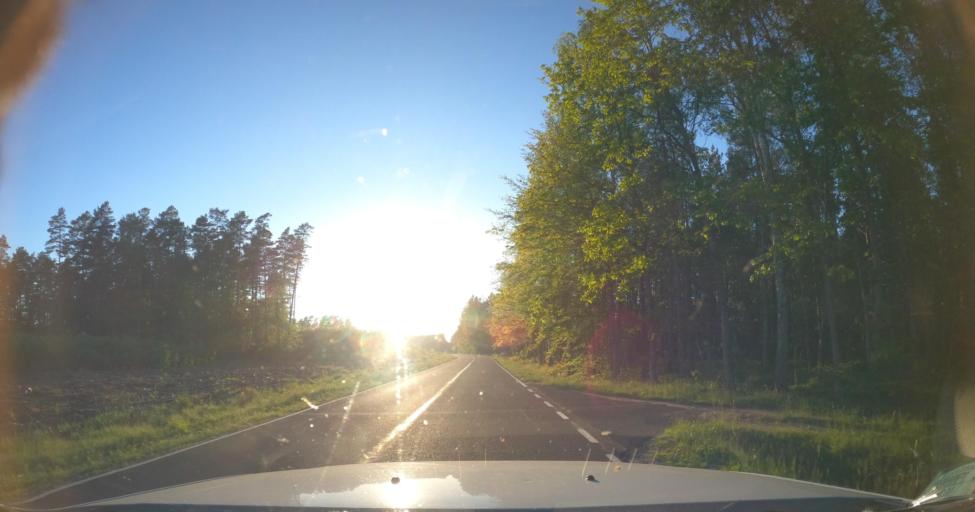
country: PL
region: Pomeranian Voivodeship
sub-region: Powiat slupski
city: Potegowo
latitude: 54.4002
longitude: 17.4614
